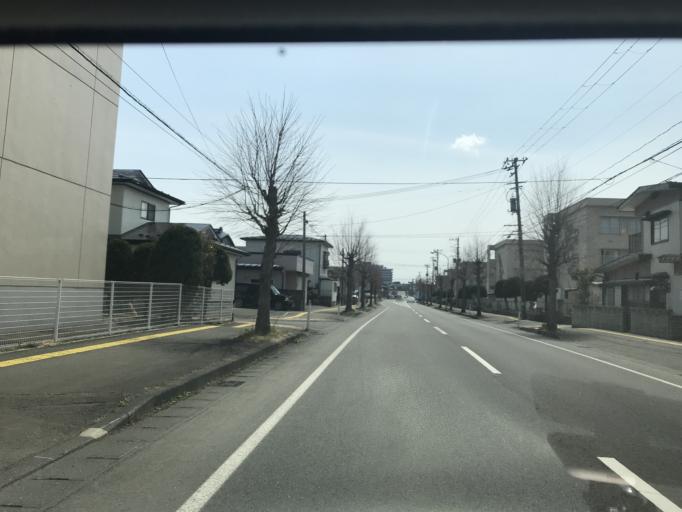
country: JP
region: Iwate
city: Mizusawa
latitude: 39.1305
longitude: 141.1361
